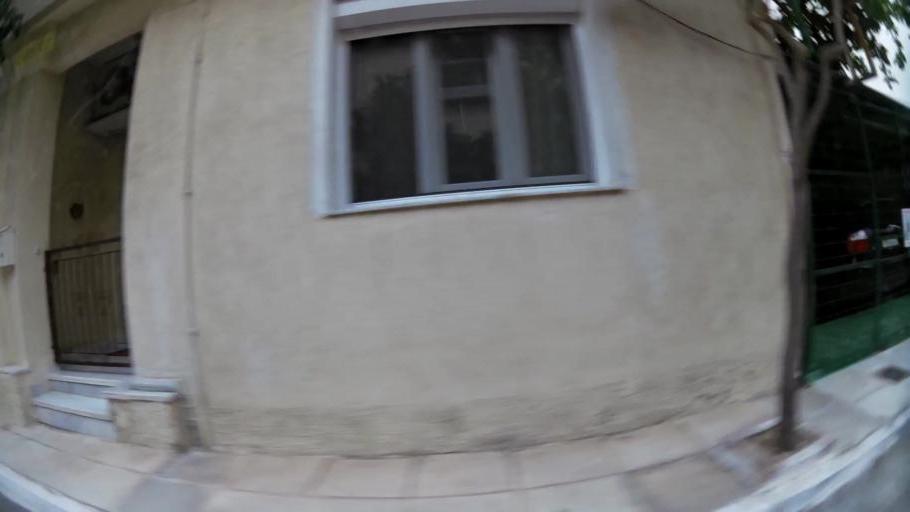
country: GR
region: Attica
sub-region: Nomarchia Athinas
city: Peristeri
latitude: 38.0036
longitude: 23.6972
